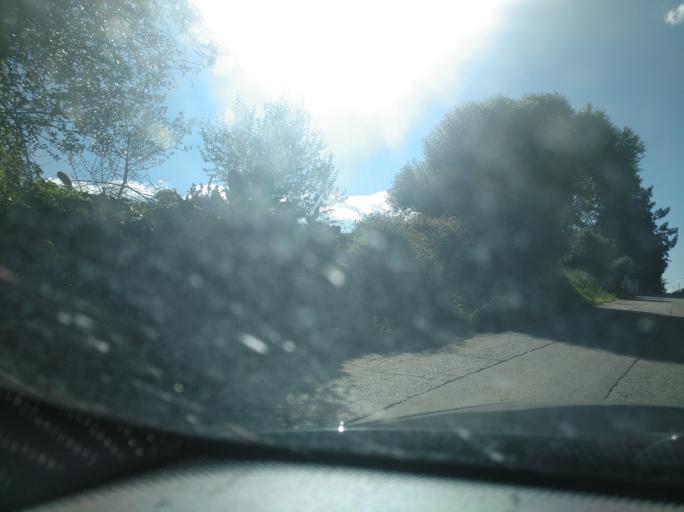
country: PT
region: Faro
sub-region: Vila Real de Santo Antonio
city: Monte Gordo
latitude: 37.1687
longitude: -7.5393
